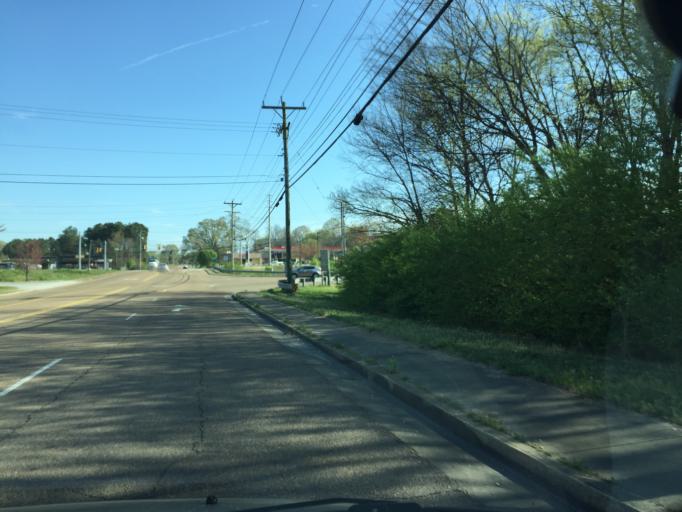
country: US
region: Tennessee
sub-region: Hamilton County
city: East Chattanooga
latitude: 35.0721
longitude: -85.1911
